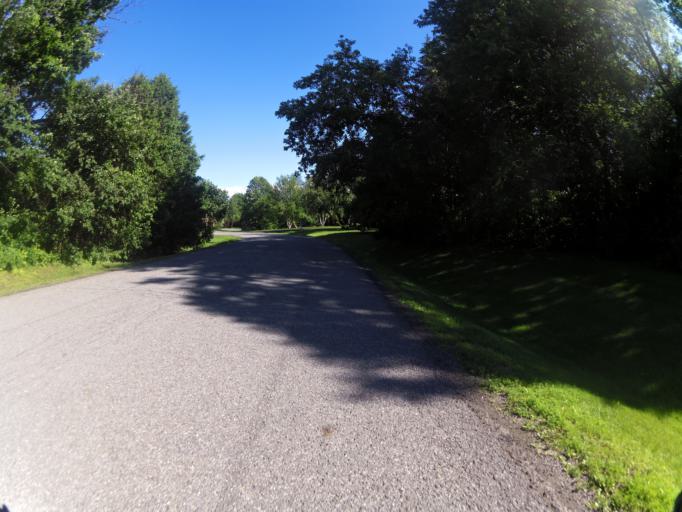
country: CA
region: Ontario
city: Bells Corners
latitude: 45.2783
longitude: -75.7919
